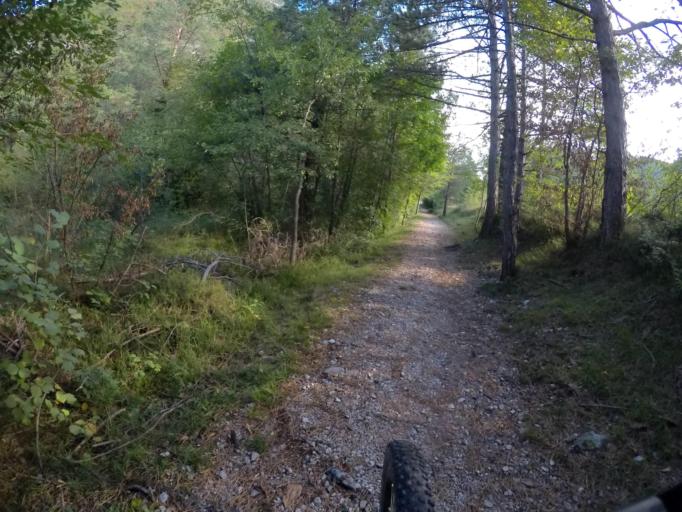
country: IT
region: Friuli Venezia Giulia
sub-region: Provincia di Udine
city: Tolmezzo
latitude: 46.4031
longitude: 13.0392
